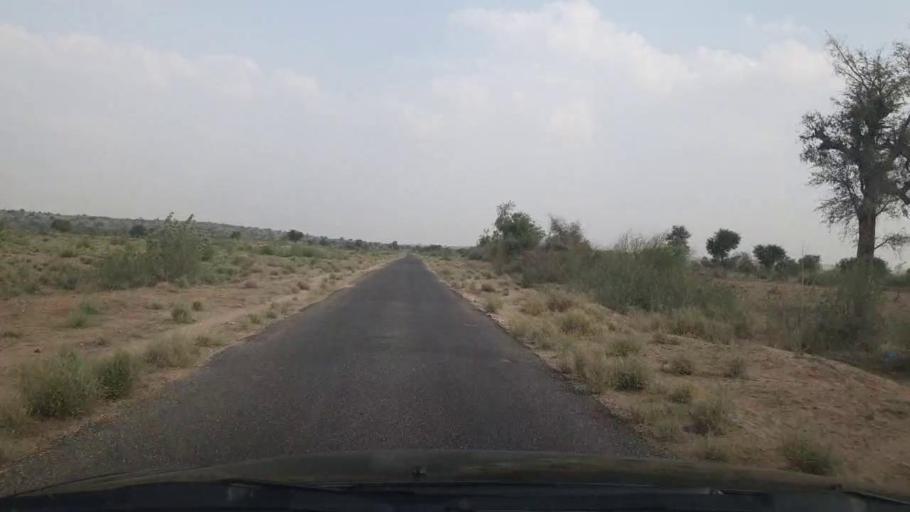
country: PK
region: Sindh
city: Islamkot
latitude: 25.0137
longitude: 70.6328
